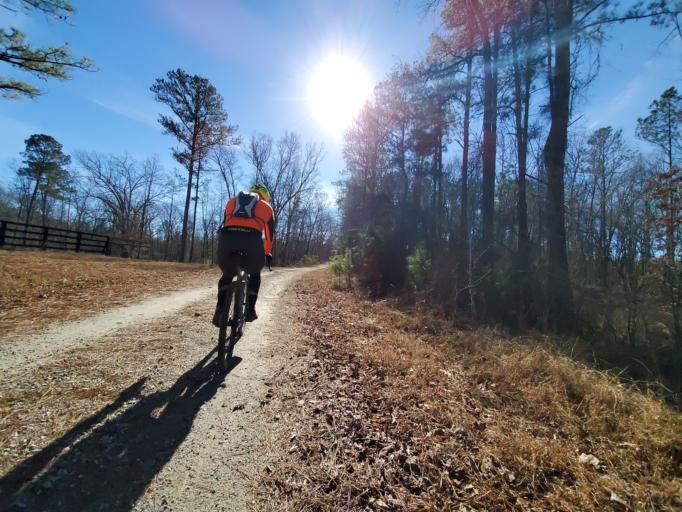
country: US
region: Georgia
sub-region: Fulton County
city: Chattahoochee Hills
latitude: 33.5694
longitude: -84.7542
